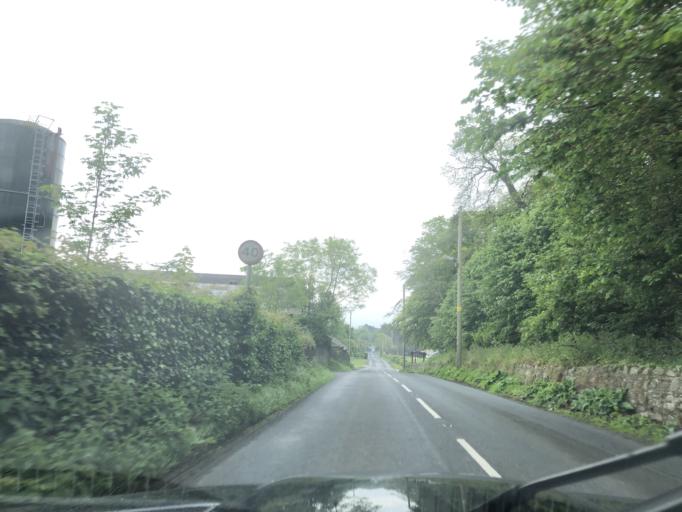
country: GB
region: Northern Ireland
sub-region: Down District
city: Newcastle
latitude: 54.2272
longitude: -5.9231
